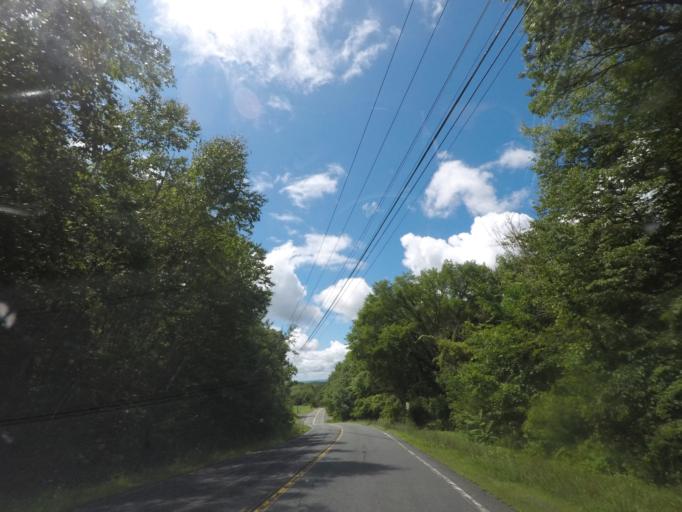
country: US
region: New York
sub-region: Rensselaer County
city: Wynantskill
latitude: 42.6685
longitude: -73.6480
